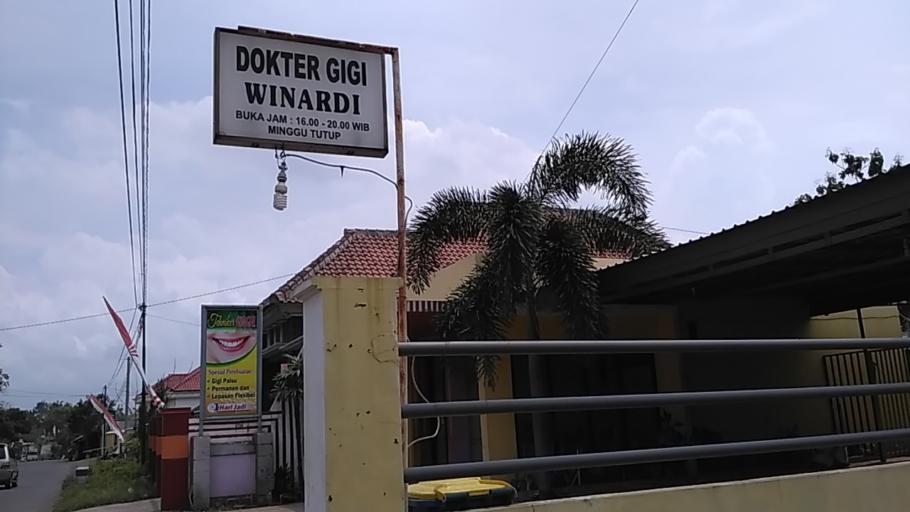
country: ID
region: East Java
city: Krajan
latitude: -8.3088
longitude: 114.2974
